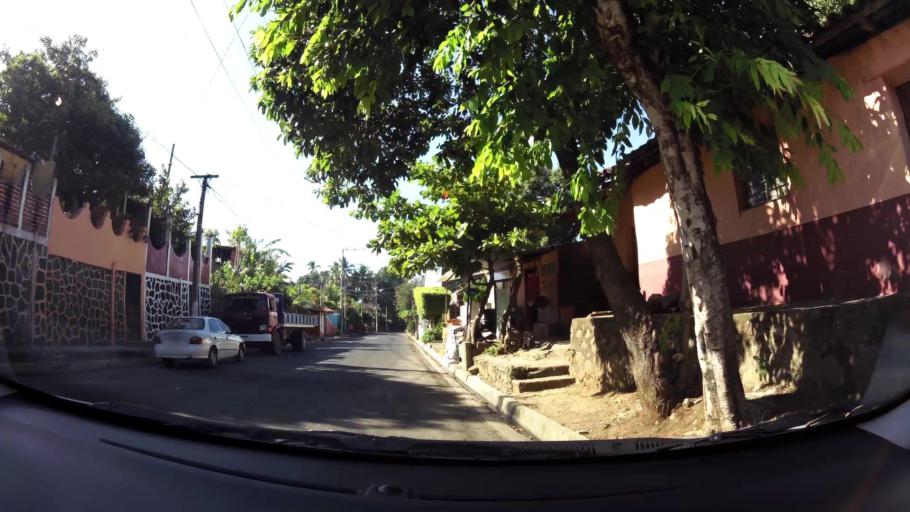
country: SV
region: Sonsonate
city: Sonzacate
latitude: 13.7357
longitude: -89.7175
